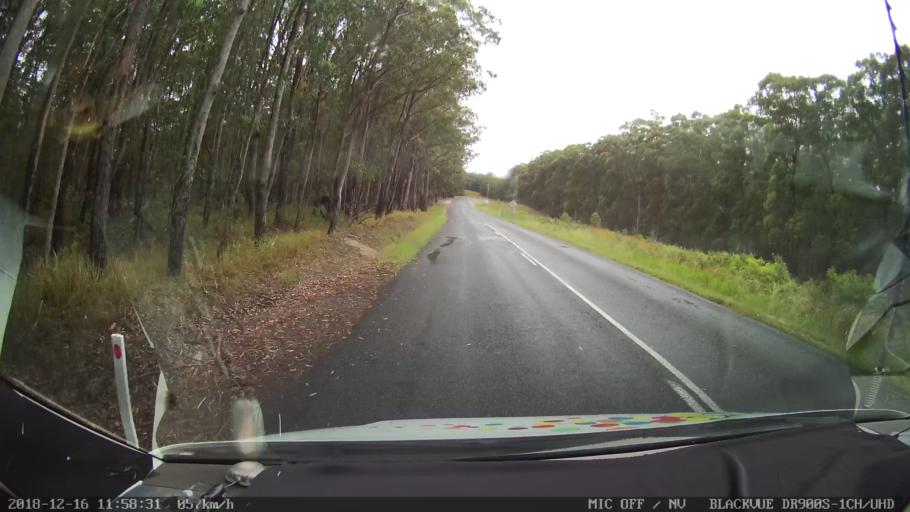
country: AU
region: New South Wales
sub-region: Tenterfield Municipality
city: Carrolls Creek
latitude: -28.9229
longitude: 152.3131
